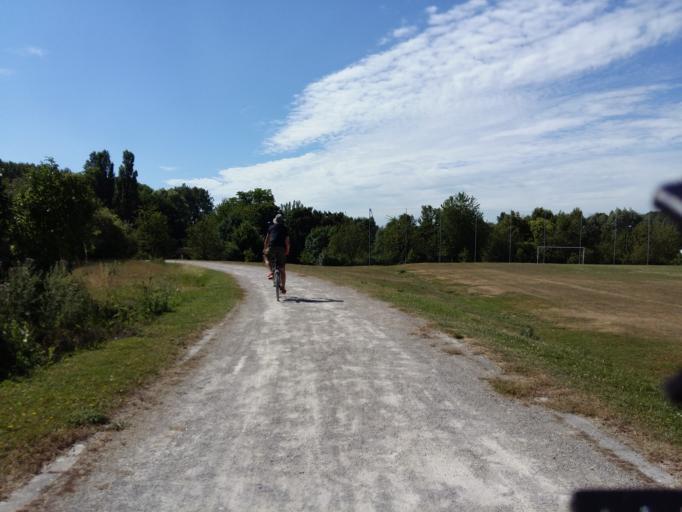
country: FR
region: Picardie
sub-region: Departement de la Somme
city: Dreuil-les-Amiens
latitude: 49.9194
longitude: 2.2603
